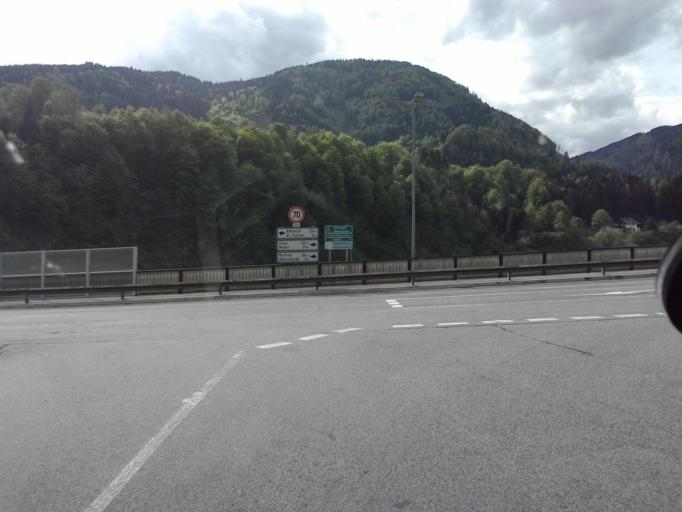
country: AT
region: Styria
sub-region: Politischer Bezirk Liezen
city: Altenmarkt bei Sankt Gallen
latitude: 47.7138
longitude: 14.6379
